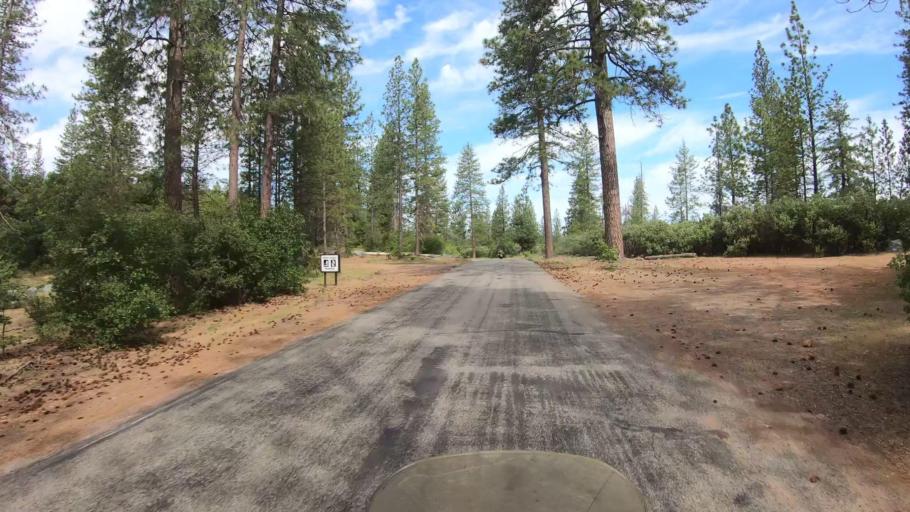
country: US
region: California
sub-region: Tuolumne County
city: Tuolumne City
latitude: 37.8396
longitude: -120.1261
